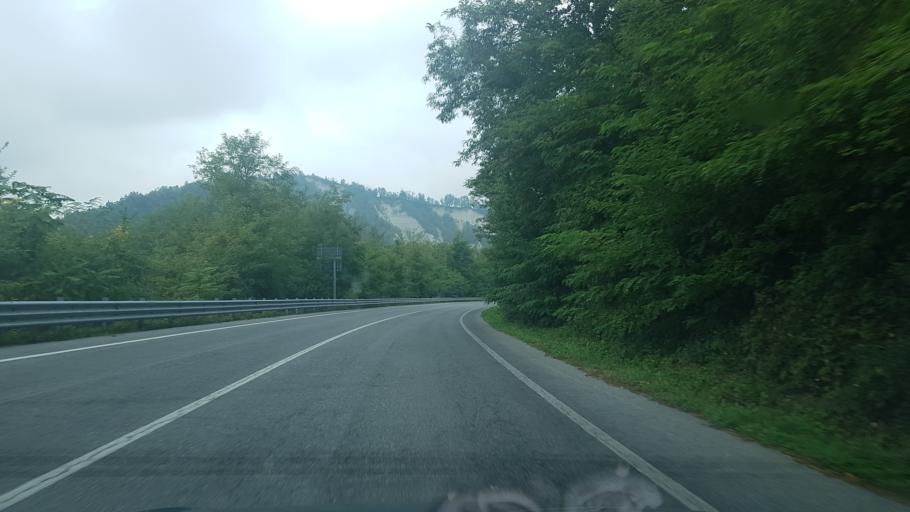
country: IT
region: Piedmont
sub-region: Provincia di Cuneo
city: Ciglie
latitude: 44.4236
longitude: 7.9357
